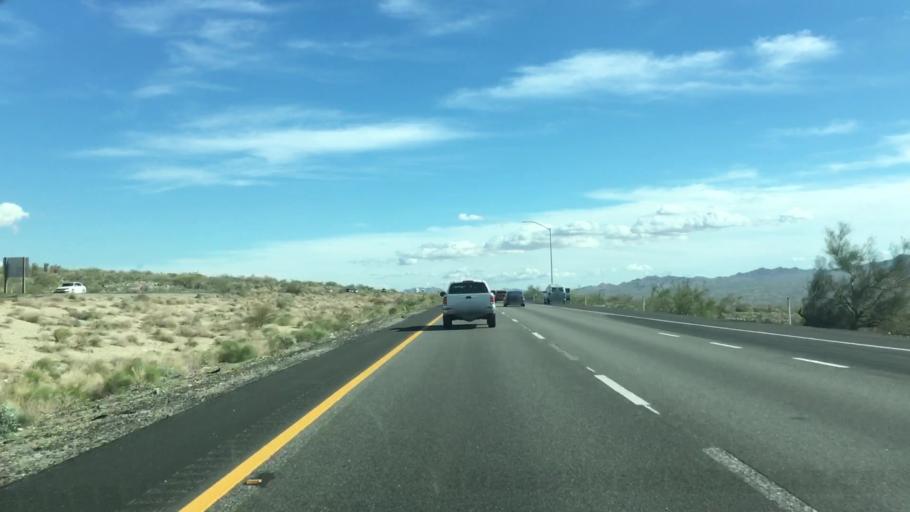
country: US
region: California
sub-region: Riverside County
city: Mecca
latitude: 33.6690
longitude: -115.9108
